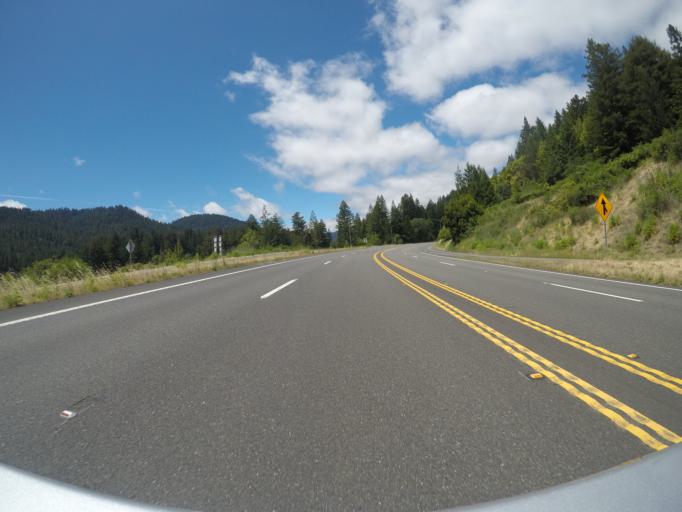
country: US
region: California
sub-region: Humboldt County
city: Redway
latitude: 40.2675
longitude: -123.8728
